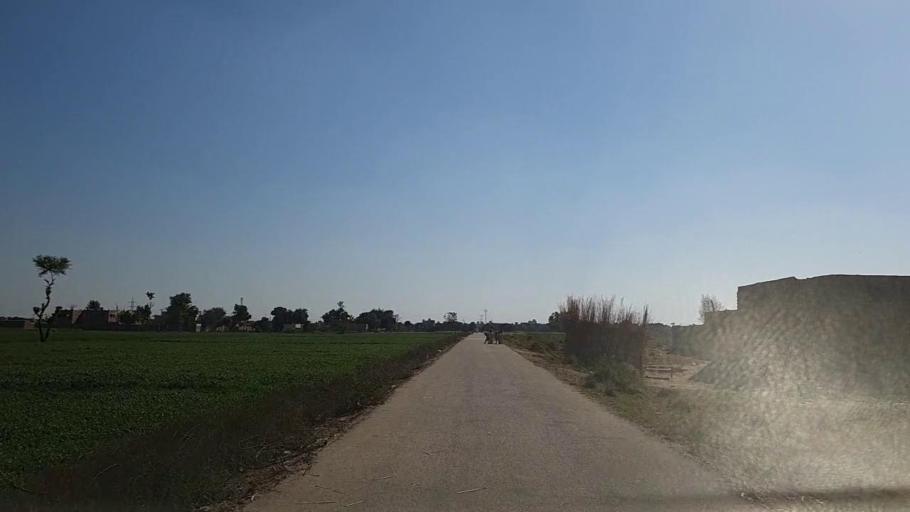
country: PK
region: Sindh
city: Nawabshah
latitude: 26.2614
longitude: 68.4242
